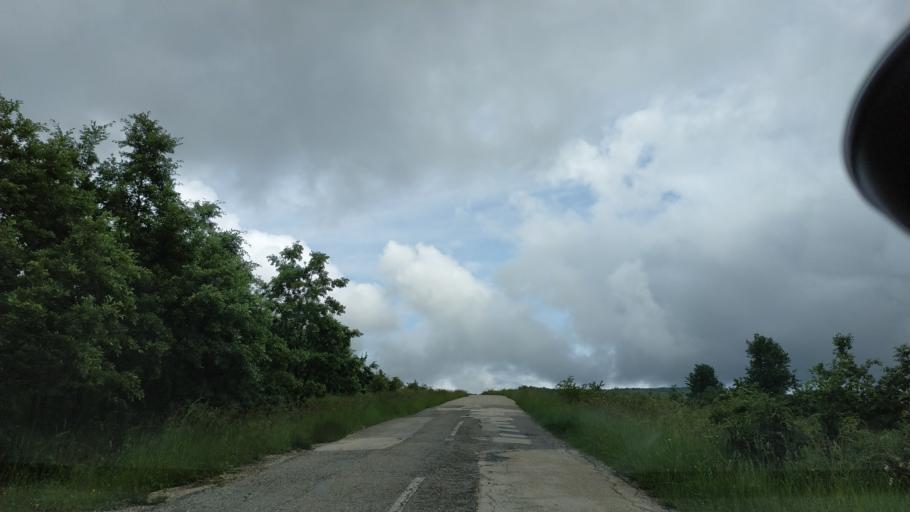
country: RS
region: Central Serbia
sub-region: Zajecarski Okrug
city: Soko Banja
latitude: 43.7031
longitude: 21.9364
